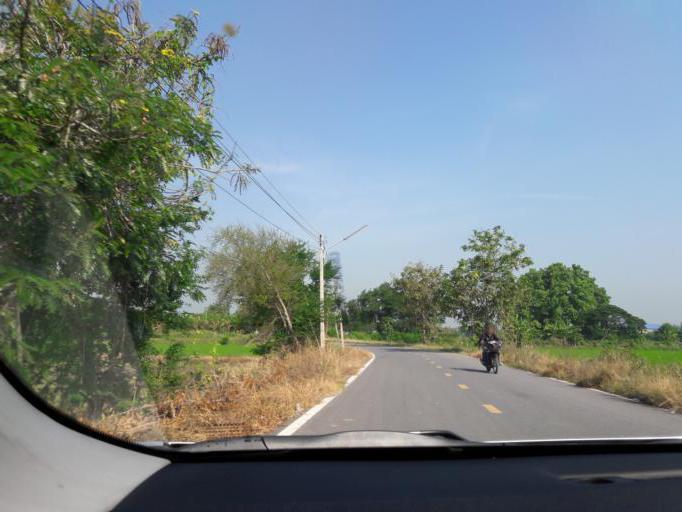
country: TH
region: Ang Thong
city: Ang Thong
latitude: 14.5915
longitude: 100.4295
